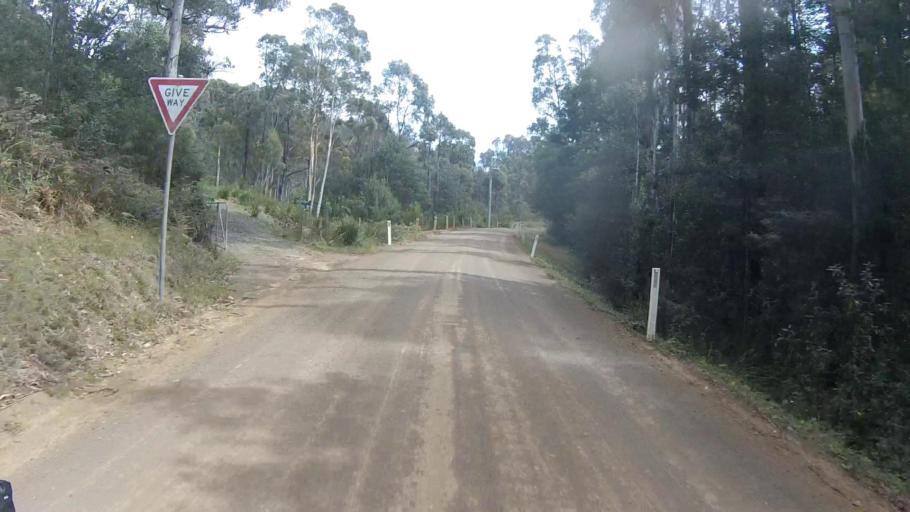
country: AU
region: Tasmania
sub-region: Sorell
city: Sorell
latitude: -42.7681
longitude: 147.8059
